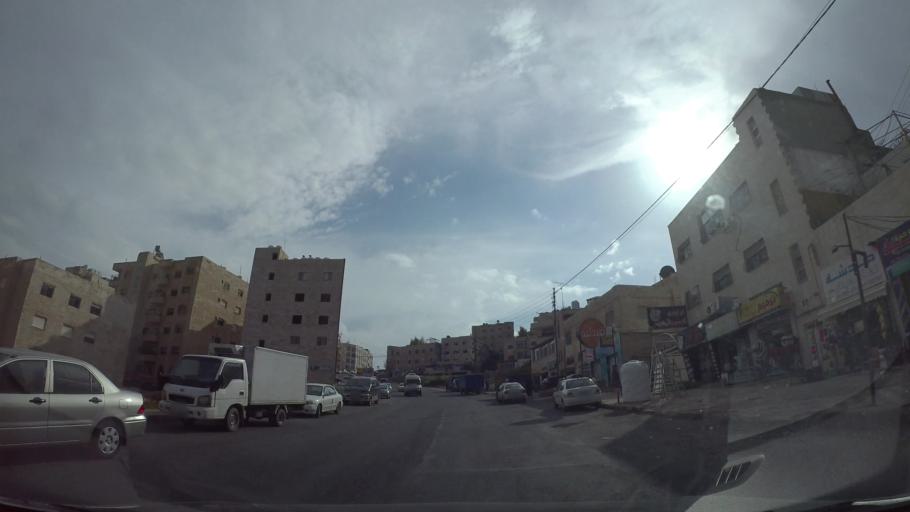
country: JO
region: Amman
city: Amman
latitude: 32.0058
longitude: 35.9506
